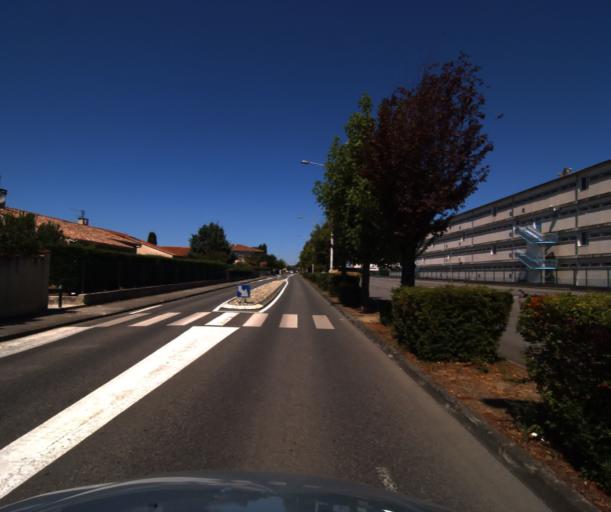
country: FR
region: Midi-Pyrenees
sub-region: Departement de la Haute-Garonne
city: Muret
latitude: 43.4530
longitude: 1.3288
